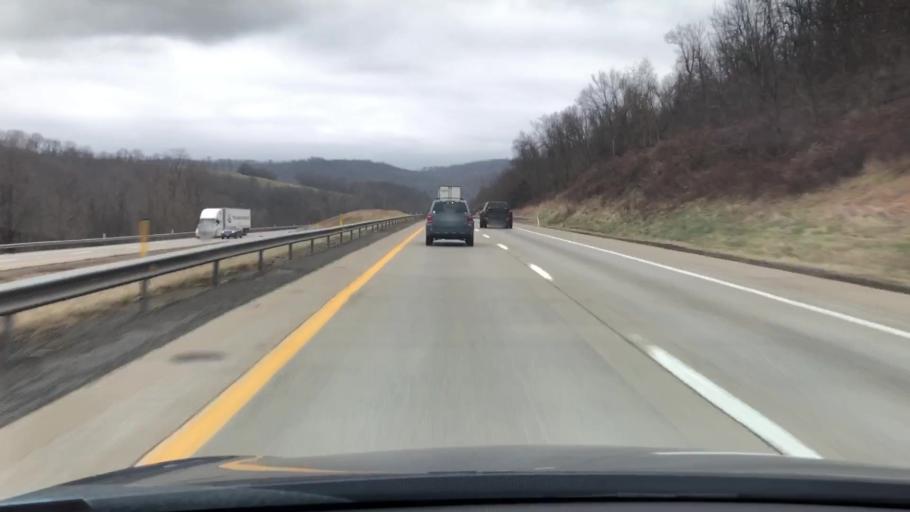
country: US
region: Pennsylvania
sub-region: Greene County
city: Waynesburg
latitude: 40.0343
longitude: -80.1779
